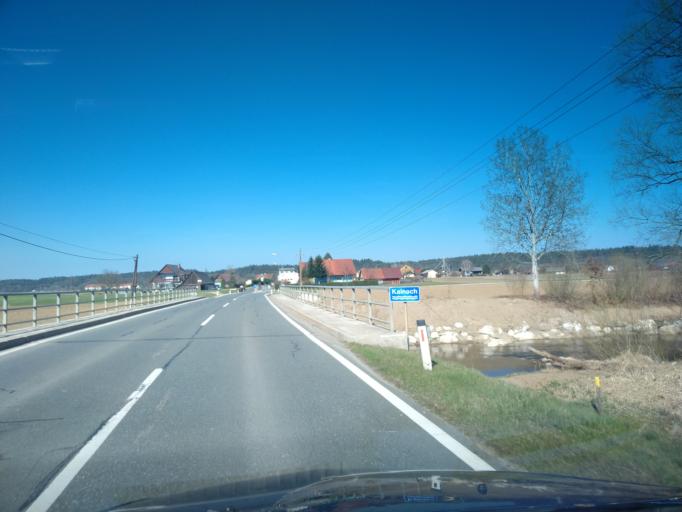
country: AT
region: Styria
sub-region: Politischer Bezirk Leibnitz
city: Hengsberg
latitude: 46.9037
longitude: 15.4078
